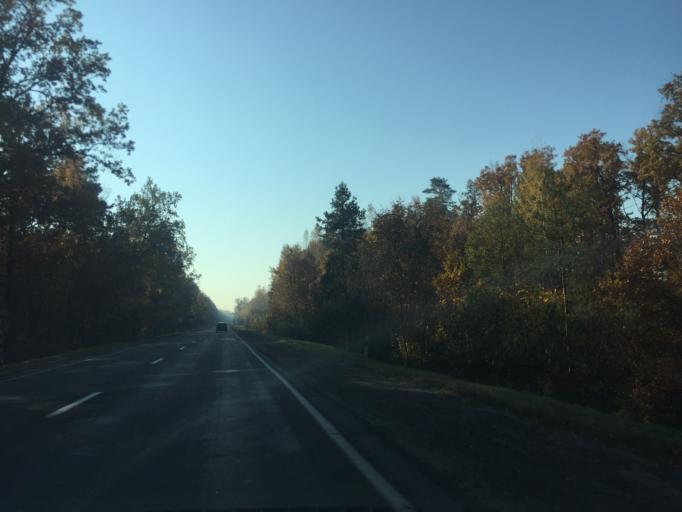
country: BY
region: Gomel
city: Gomel
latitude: 52.4100
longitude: 30.8288
